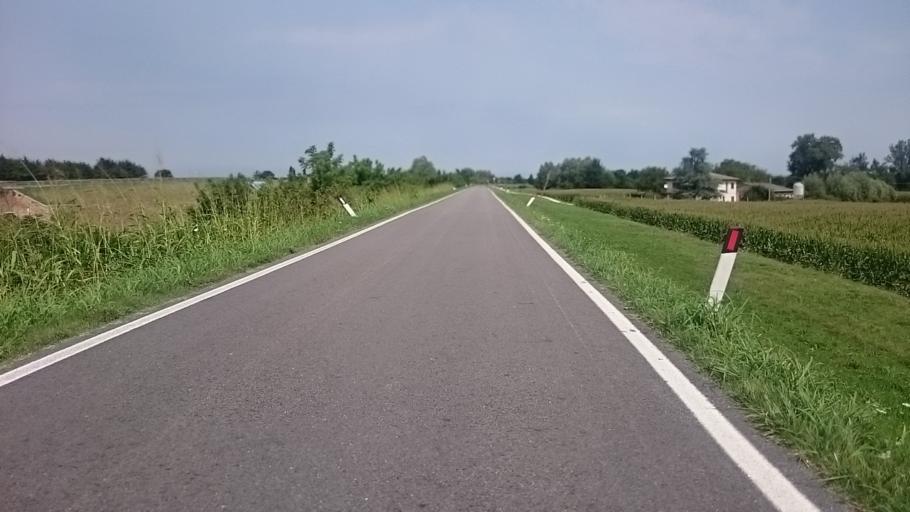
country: IT
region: Veneto
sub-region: Provincia di Padova
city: Polverara
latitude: 45.3267
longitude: 11.9403
